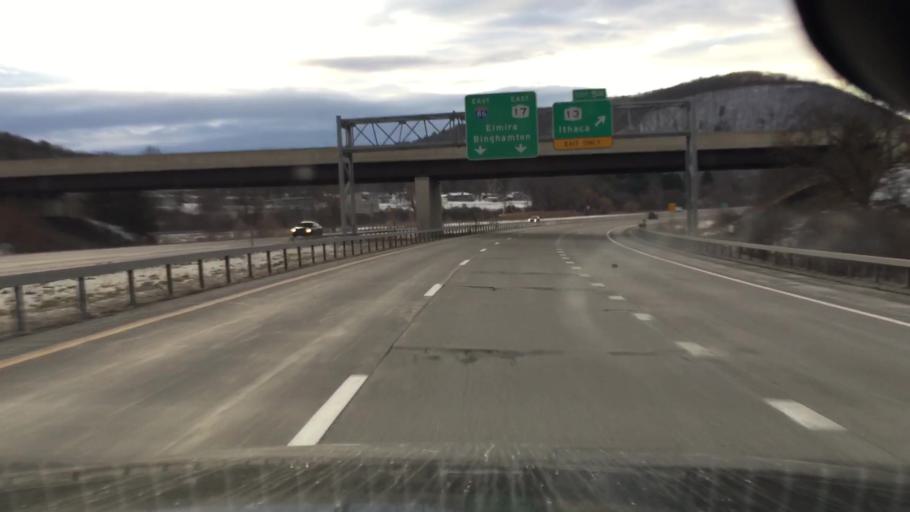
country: US
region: New York
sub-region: Chemung County
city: Horseheads
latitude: 42.1533
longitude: -76.8086
